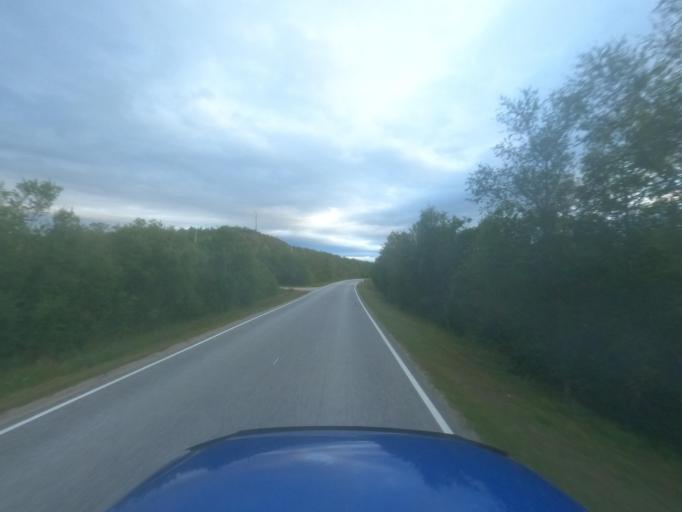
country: NO
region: Finnmark Fylke
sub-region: Porsanger
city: Lakselv
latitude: 70.0211
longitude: 24.9670
